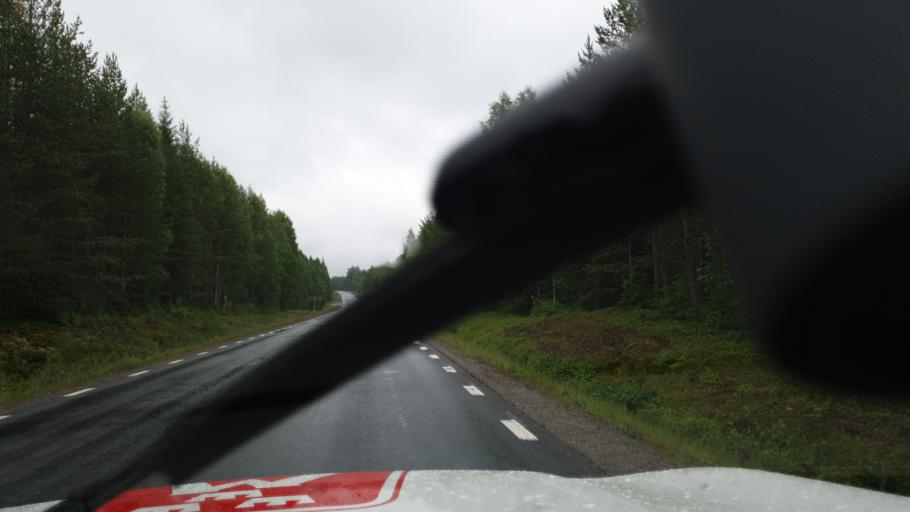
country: SE
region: Vaesterbotten
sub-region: Vannas Kommun
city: Vaennaes
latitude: 63.7718
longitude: 19.6944
